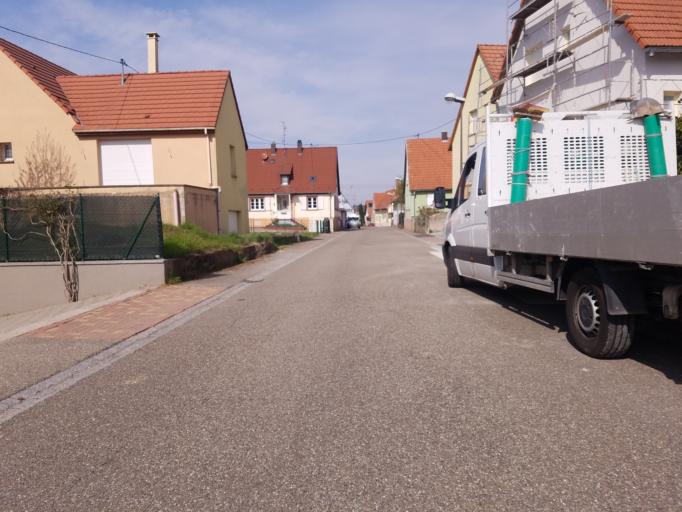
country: FR
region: Alsace
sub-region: Departement du Bas-Rhin
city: Betschdorf
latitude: 48.9015
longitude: 7.9700
